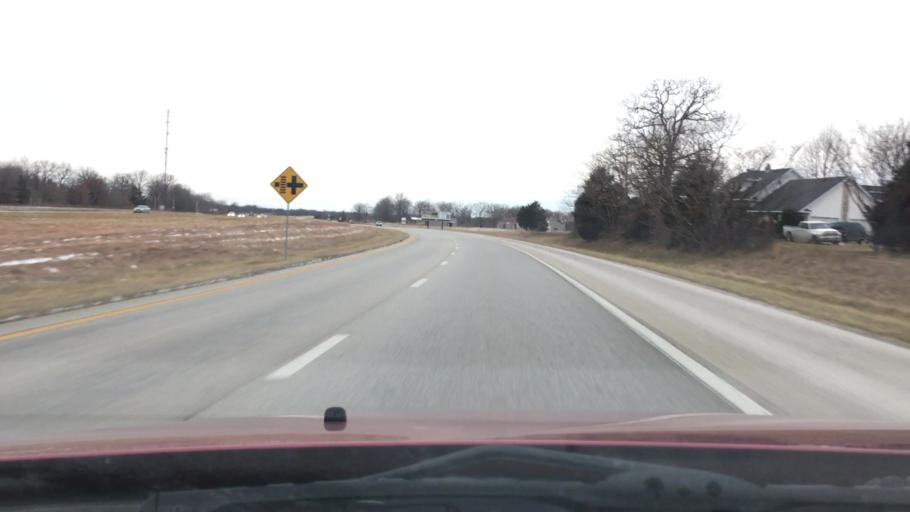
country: US
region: Missouri
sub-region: Webster County
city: Seymour
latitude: 37.1691
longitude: -92.8088
